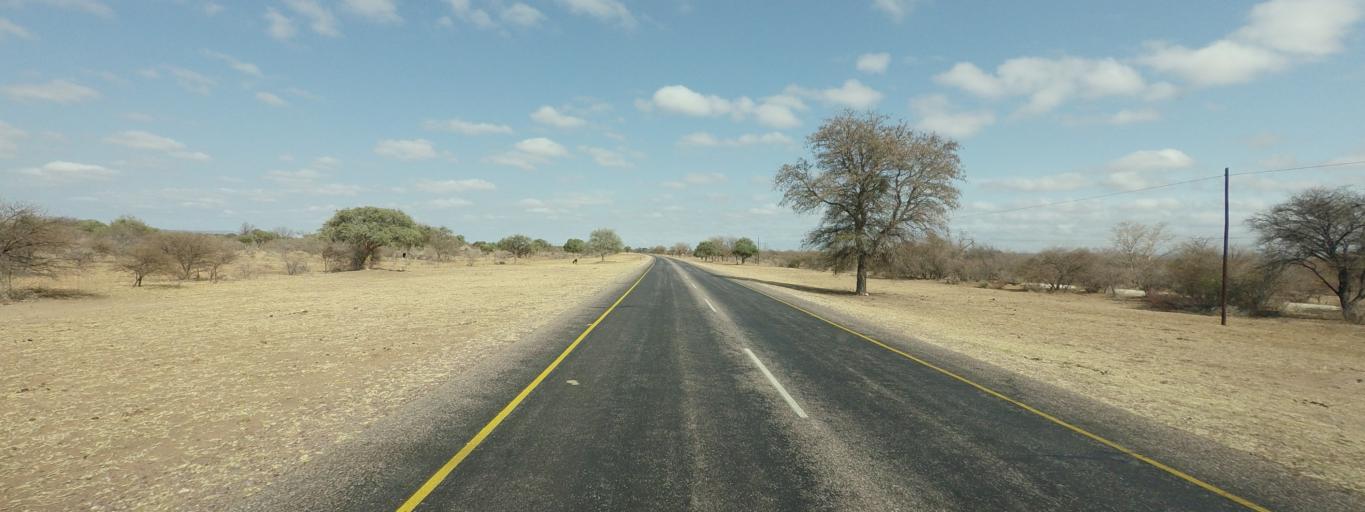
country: BW
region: Central
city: Ratholo
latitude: -22.8056
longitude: 27.5217
